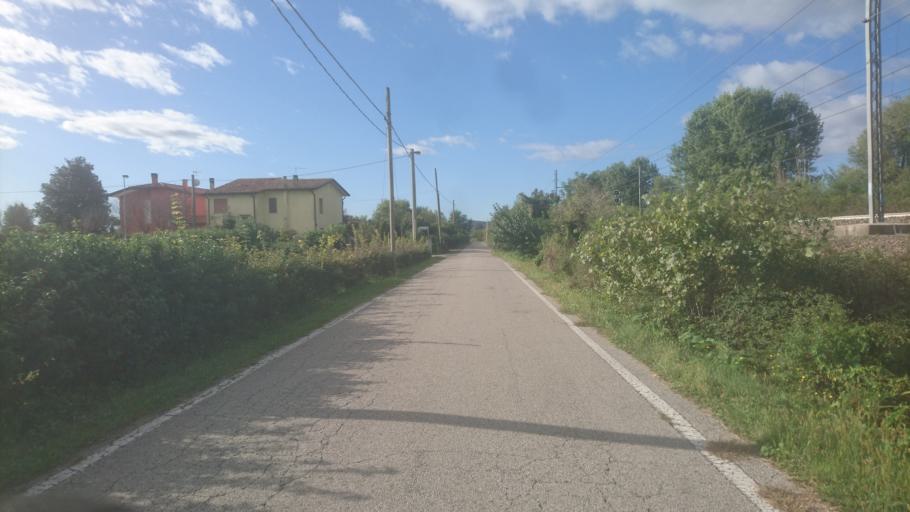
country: IT
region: Veneto
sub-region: Provincia di Padova
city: Abano Terme
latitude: 45.3500
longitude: 11.8084
